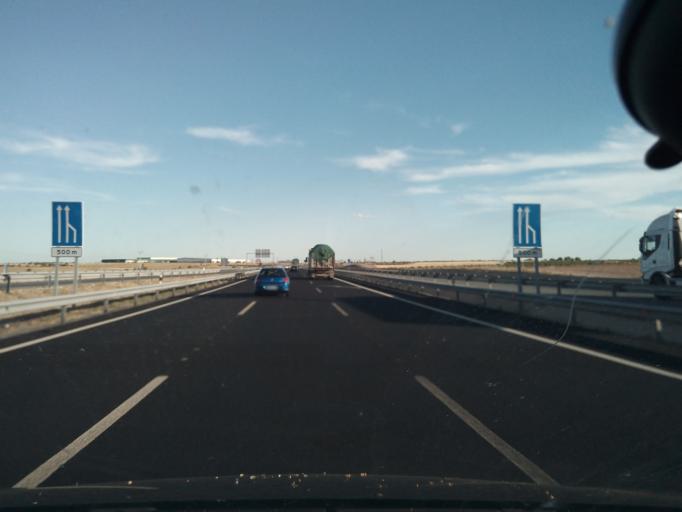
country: ES
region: Castille-La Mancha
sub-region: Province of Toledo
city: Dosbarrios
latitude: 39.9065
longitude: -3.4749
